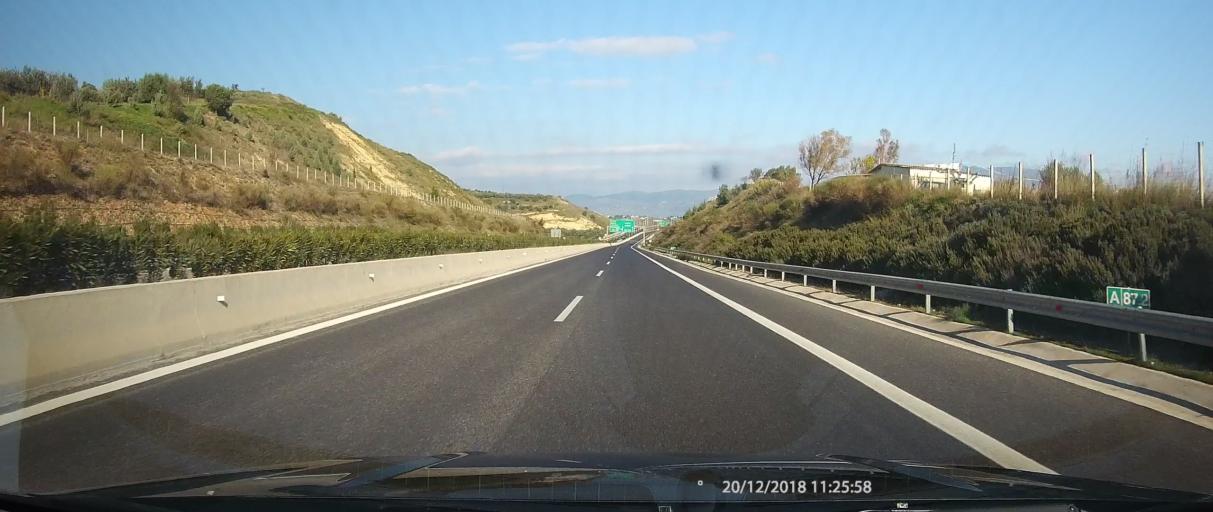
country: GR
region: Peloponnese
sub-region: Nomos Korinthias
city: Arkhaia Korinthos
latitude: 37.9080
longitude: 22.9062
